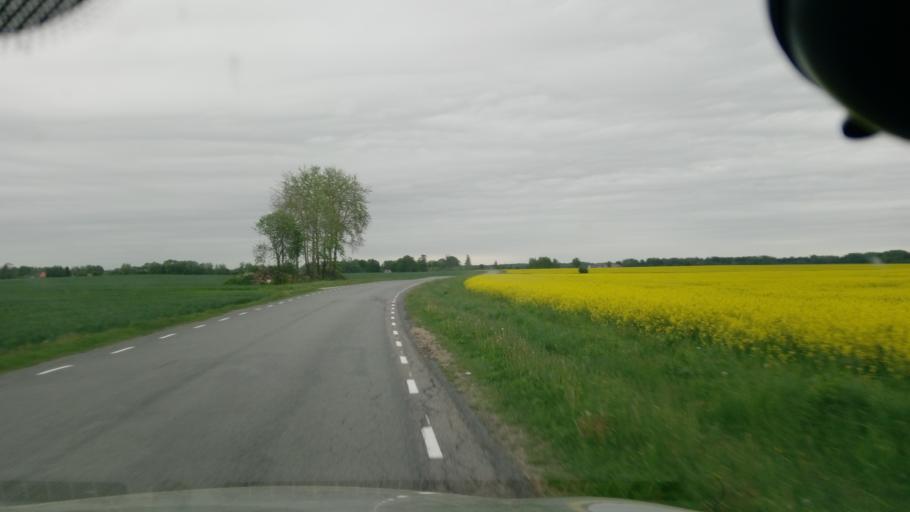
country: EE
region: Jaervamaa
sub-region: Koeru vald
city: Koeru
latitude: 58.9978
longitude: 26.0664
